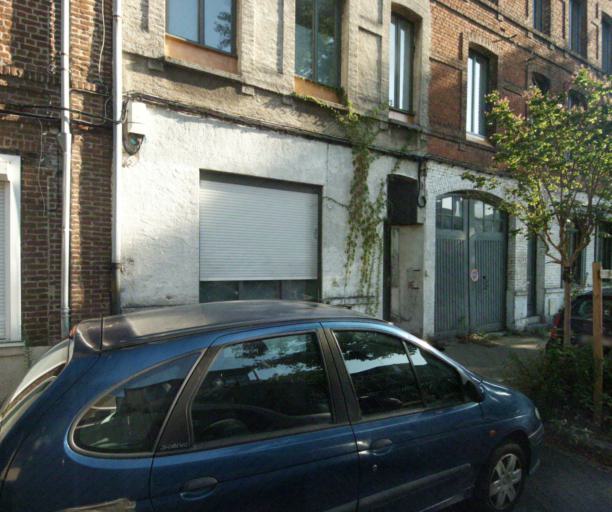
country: FR
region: Nord-Pas-de-Calais
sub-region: Departement du Nord
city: Lille
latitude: 50.6195
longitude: 3.0551
